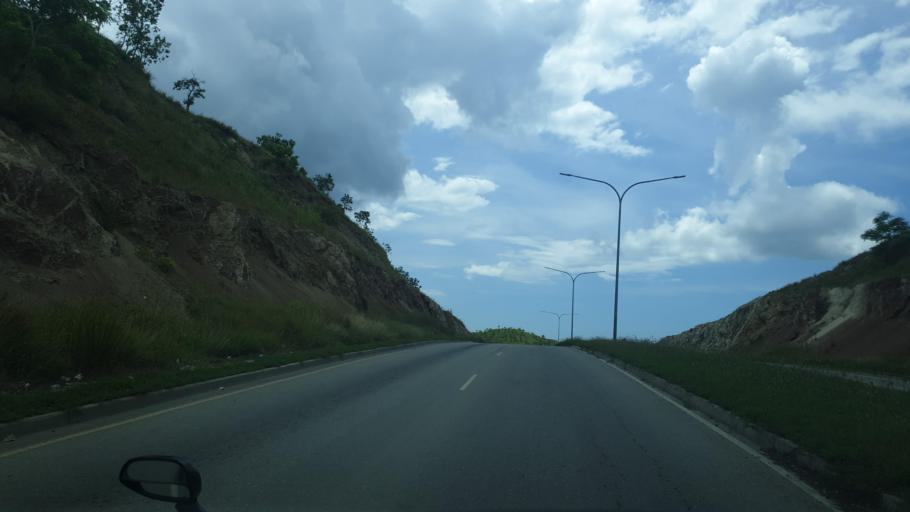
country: PG
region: National Capital
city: Port Moresby
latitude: -9.4236
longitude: 147.1398
